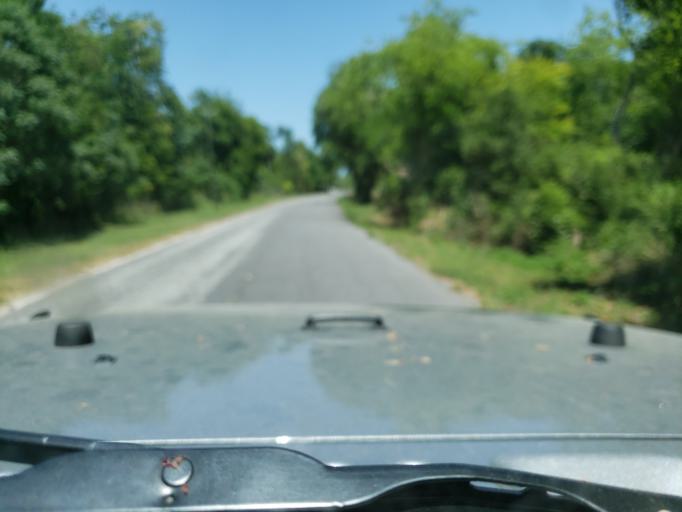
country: US
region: Georgia
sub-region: Chatham County
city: Thunderbolt
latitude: 32.0801
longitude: -81.0390
